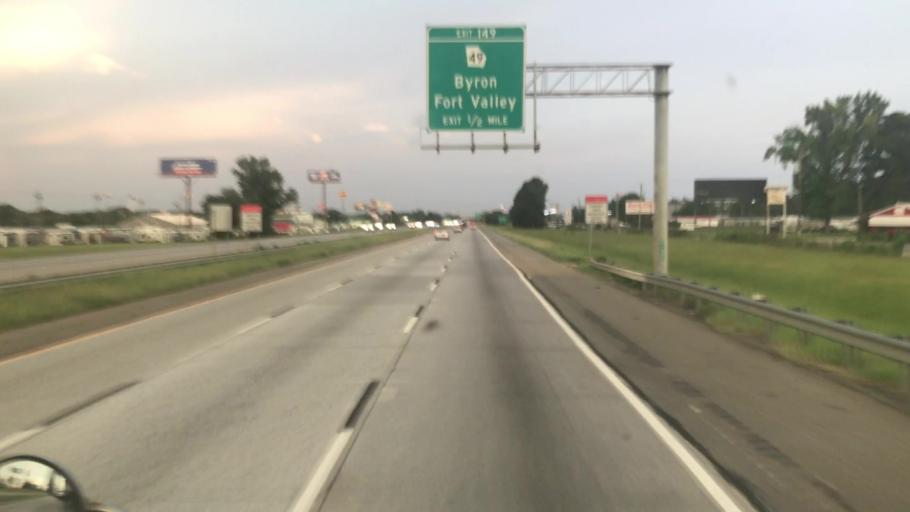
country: US
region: Georgia
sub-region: Peach County
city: Byron
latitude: 32.6691
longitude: -83.7447
